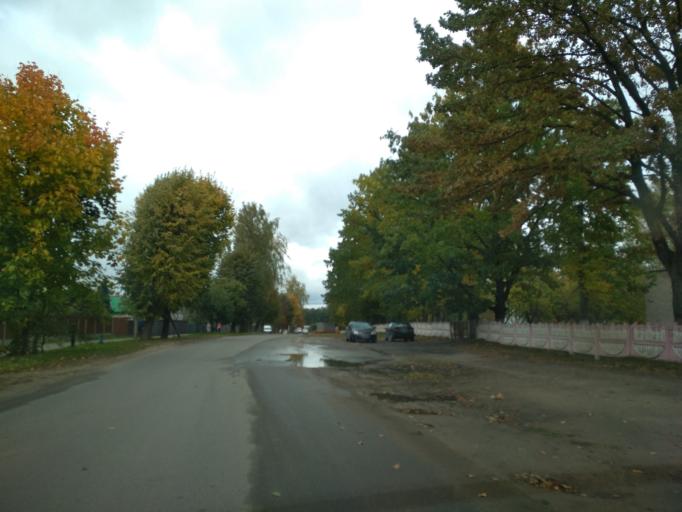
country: BY
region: Minsk
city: Mar''ina Horka
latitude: 53.5167
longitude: 28.1538
